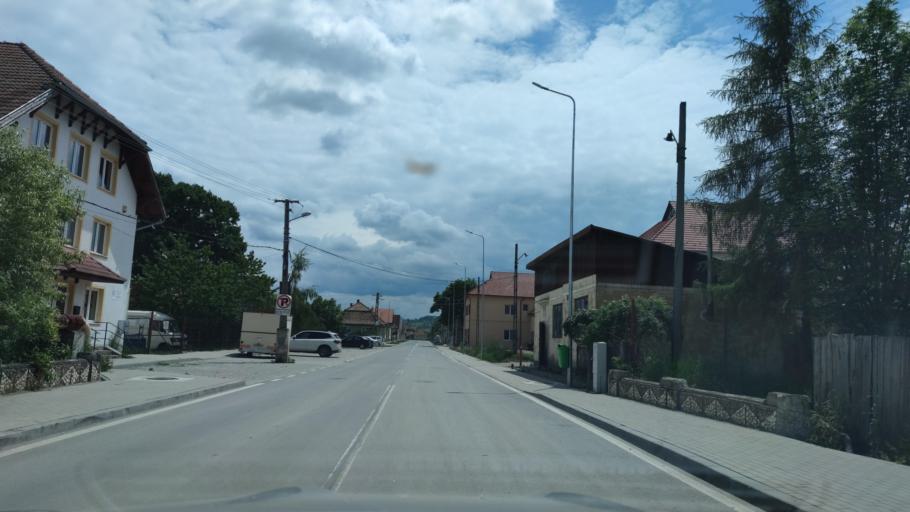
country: RO
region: Harghita
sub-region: Municipiul Gheorgheni
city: Gheorgheni
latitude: 46.7190
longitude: 25.5961
